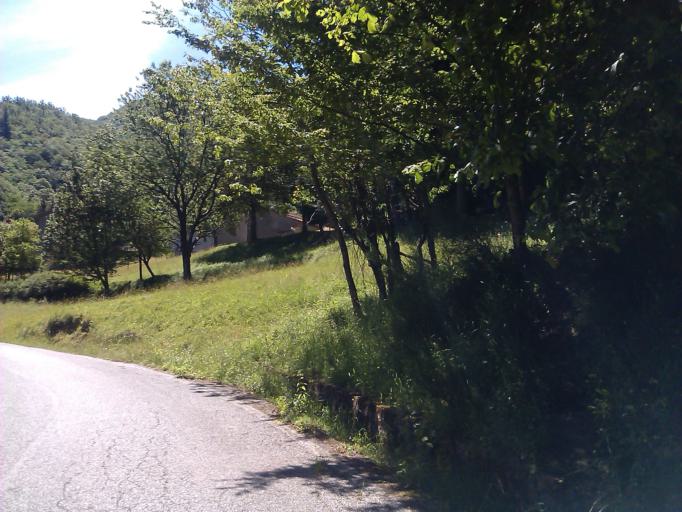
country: IT
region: Tuscany
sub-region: Provincia di Prato
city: Cantagallo
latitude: 44.0536
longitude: 11.0445
